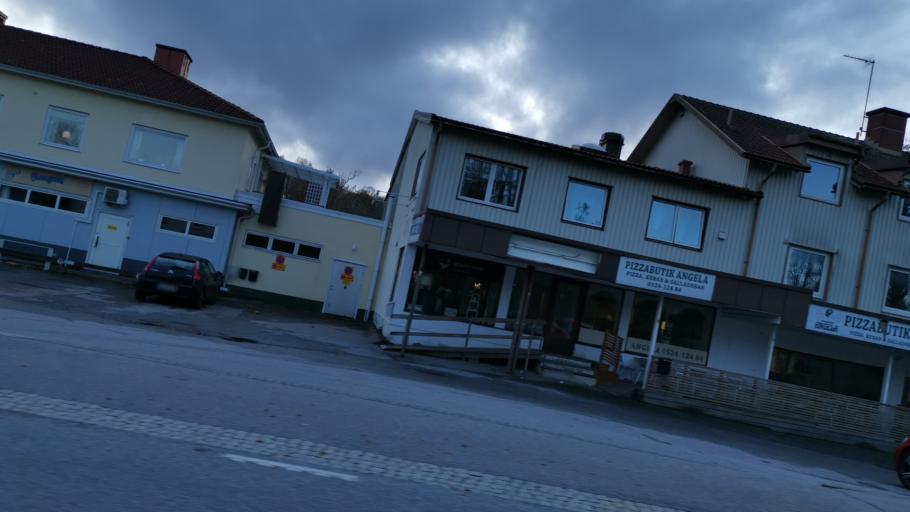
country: SE
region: Vaestra Goetaland
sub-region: Munkedals Kommun
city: Munkedal
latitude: 58.4683
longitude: 11.6731
